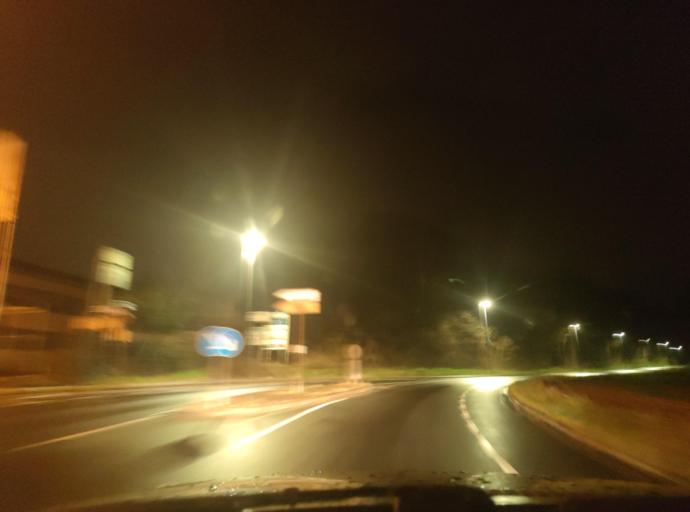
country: DE
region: North Rhine-Westphalia
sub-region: Regierungsbezirk Munster
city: Gelsenkirchen
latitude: 51.4630
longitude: 7.0991
